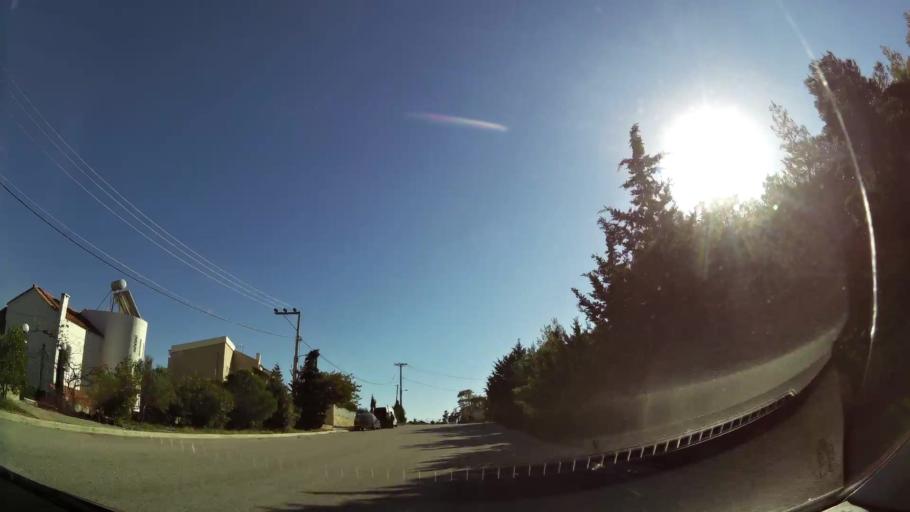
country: GR
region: Attica
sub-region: Nomarchia Anatolikis Attikis
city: Dhrafi
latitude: 38.0324
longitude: 23.8954
